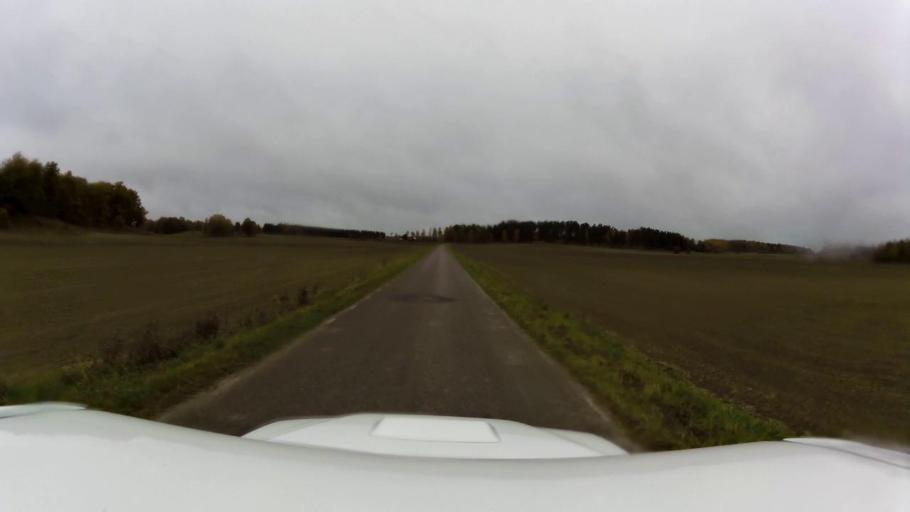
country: SE
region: OEstergoetland
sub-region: Norrkopings Kommun
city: Kimstad
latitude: 58.3933
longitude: 15.9491
